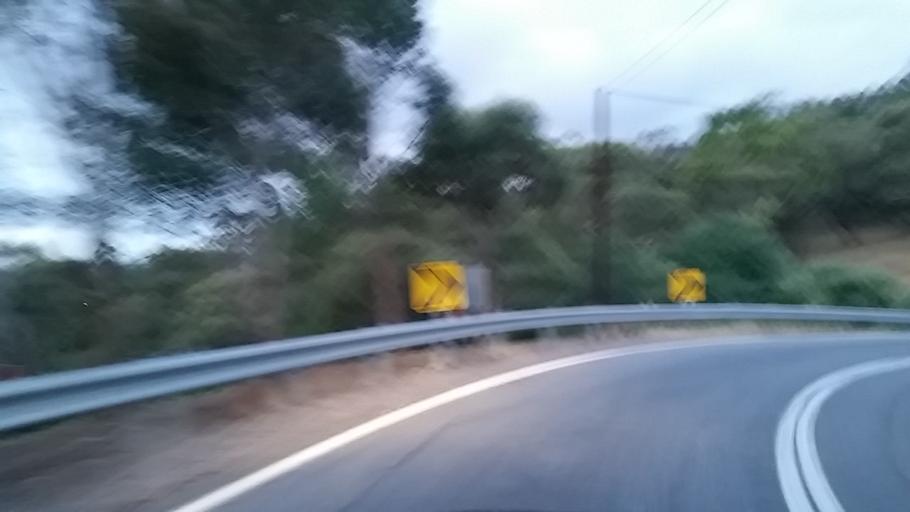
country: AU
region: South Australia
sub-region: Burnside
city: Beaumont
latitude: -34.9438
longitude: 138.6719
